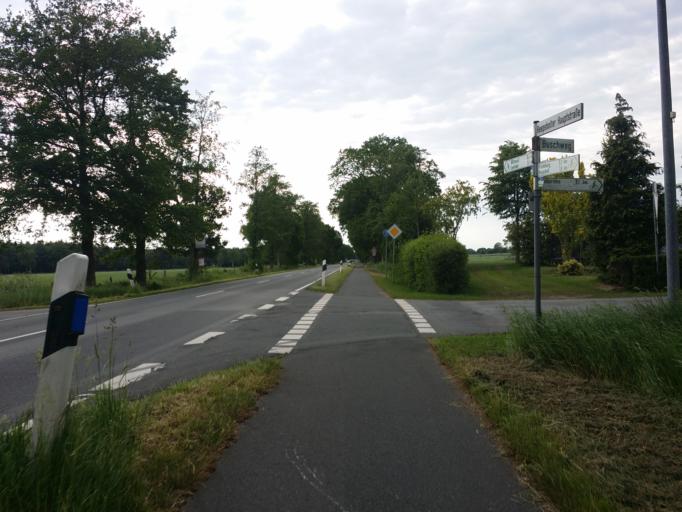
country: DE
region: Lower Saxony
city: Friedeburg
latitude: 53.5002
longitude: 7.8193
